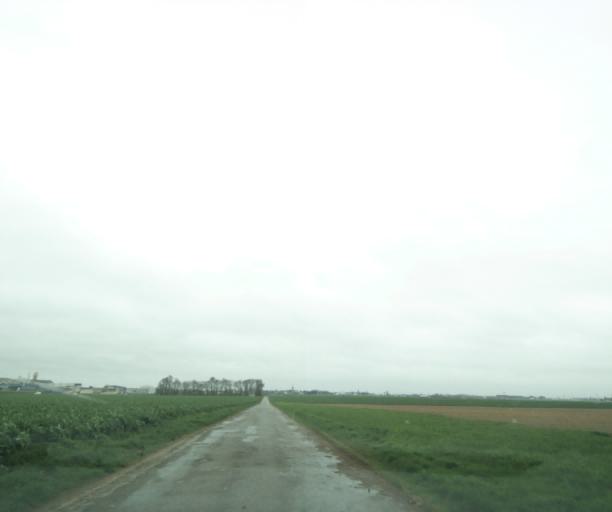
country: FR
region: Centre
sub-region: Departement du Loiret
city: Artenay
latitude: 48.0967
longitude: 1.8770
